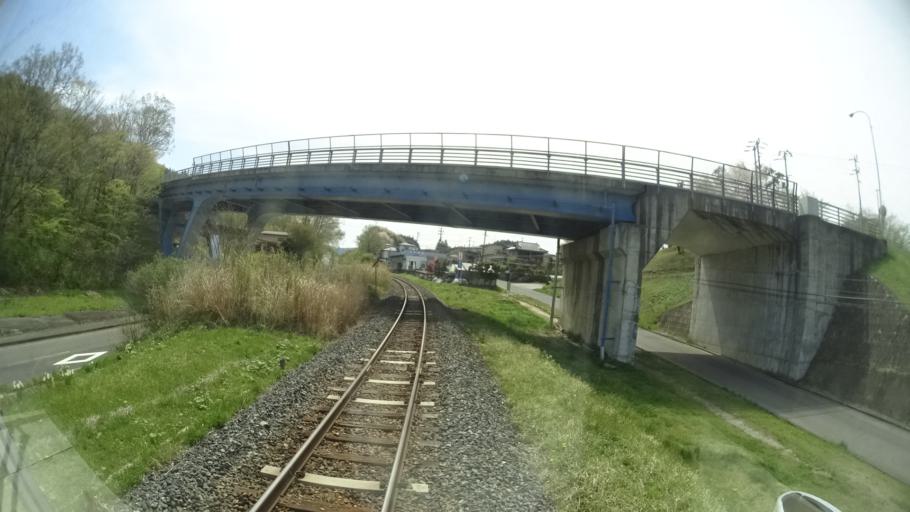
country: JP
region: Iwate
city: Ichinoseki
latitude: 38.9994
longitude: 141.2682
